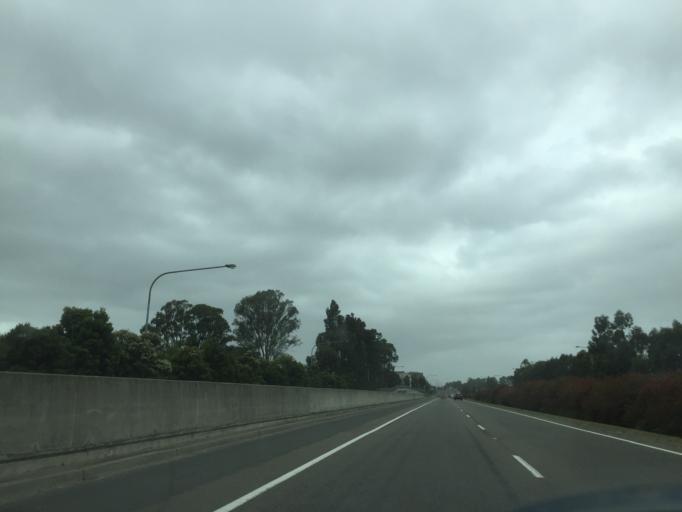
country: AU
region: New South Wales
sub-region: Blacktown
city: Stanhope Gardens
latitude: -33.7288
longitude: 150.9417
